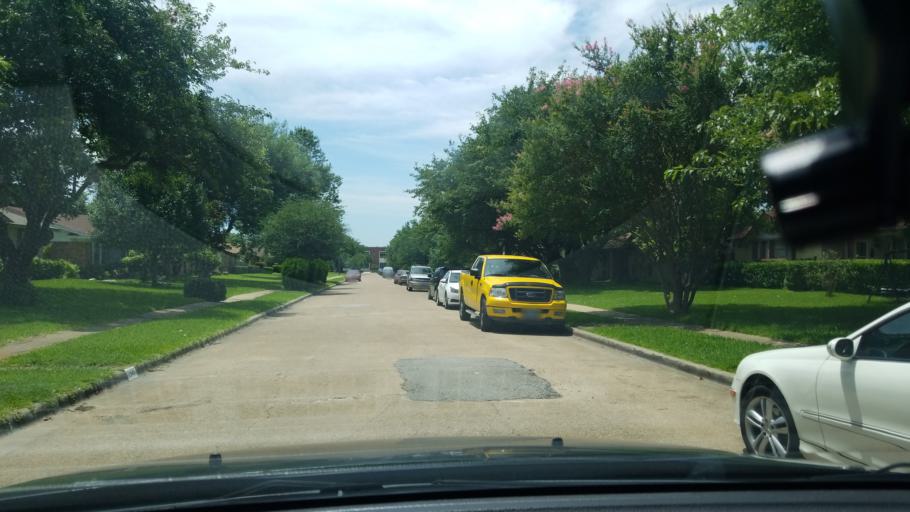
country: US
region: Texas
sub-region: Dallas County
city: Mesquite
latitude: 32.8036
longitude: -96.6591
